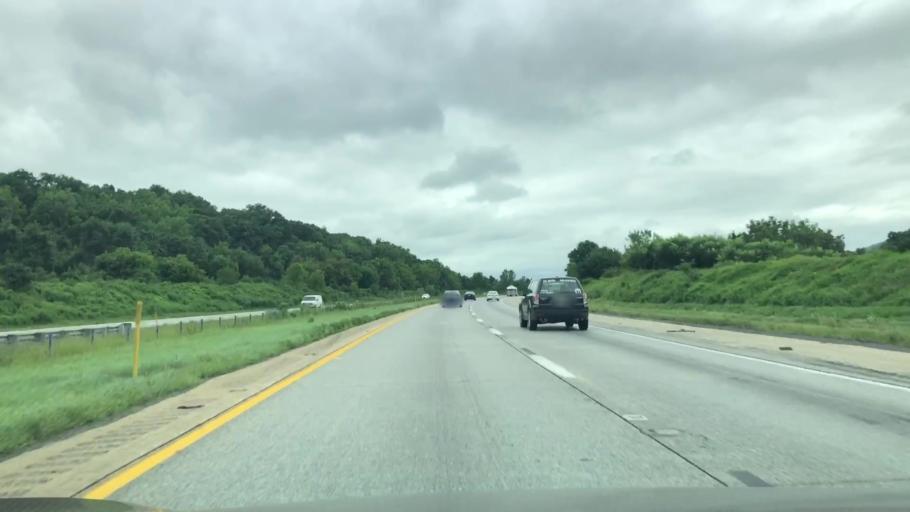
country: US
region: Pennsylvania
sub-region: Northampton County
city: Hellertown
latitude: 40.5982
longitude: -75.3202
